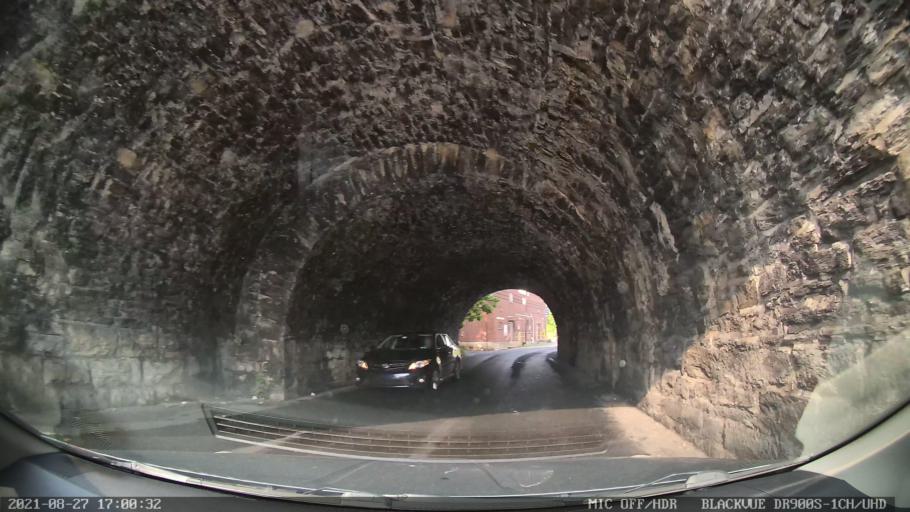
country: US
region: Pennsylvania
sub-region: Berks County
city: Hyde Park
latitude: 40.3639
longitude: -75.9253
